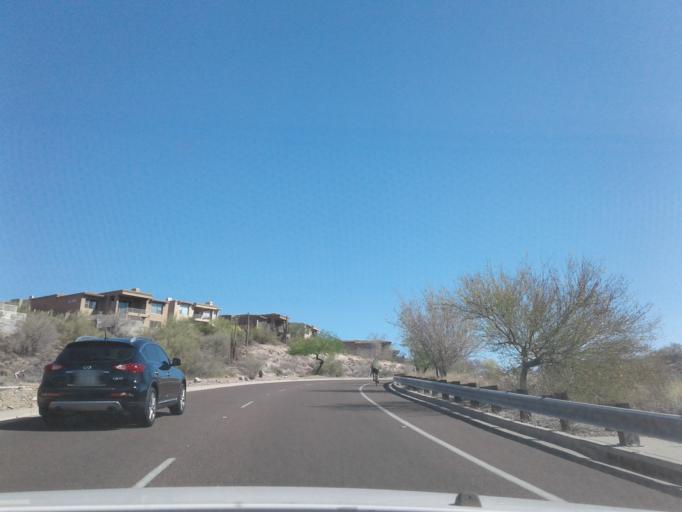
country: US
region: Arizona
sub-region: Maricopa County
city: Fountain Hills
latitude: 33.5825
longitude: -111.7576
